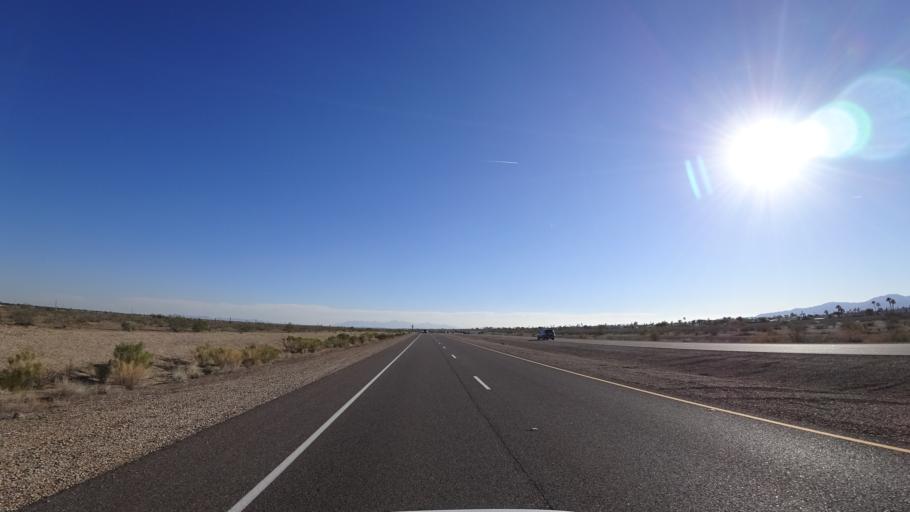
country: US
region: Arizona
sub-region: Maricopa County
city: Sun City West
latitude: 33.6705
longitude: -112.3228
